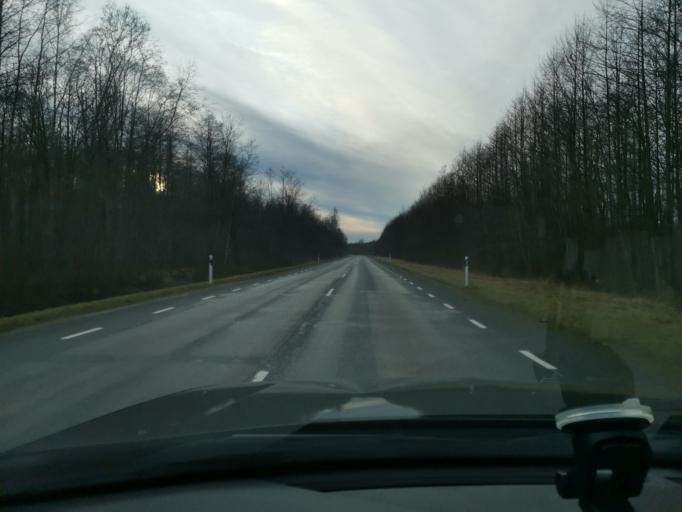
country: EE
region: Ida-Virumaa
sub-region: Narva-Joesuu linn
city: Narva-Joesuu
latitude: 59.3258
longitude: 27.9265
